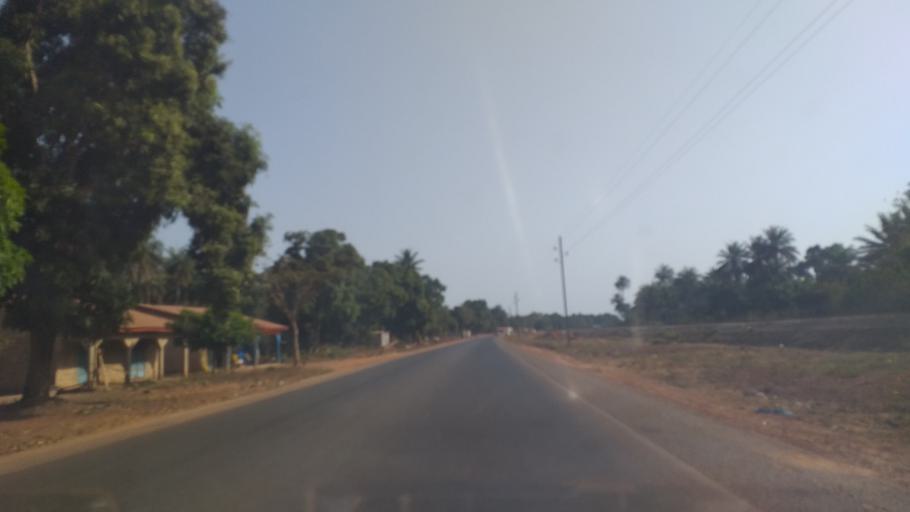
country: GN
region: Boke
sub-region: Boke Prefecture
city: Kamsar
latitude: 10.7347
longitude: -14.5162
